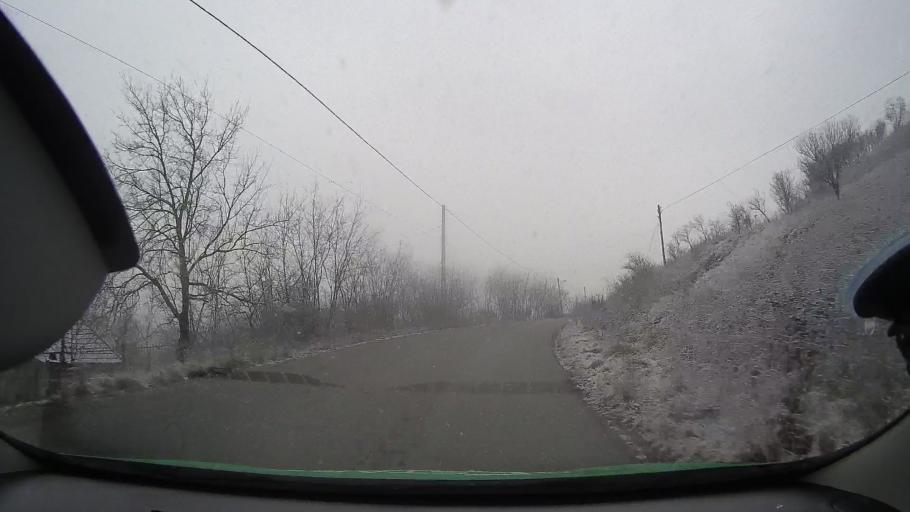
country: RO
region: Alba
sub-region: Comuna Noslac
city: Noslac
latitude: 46.3518
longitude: 23.9336
